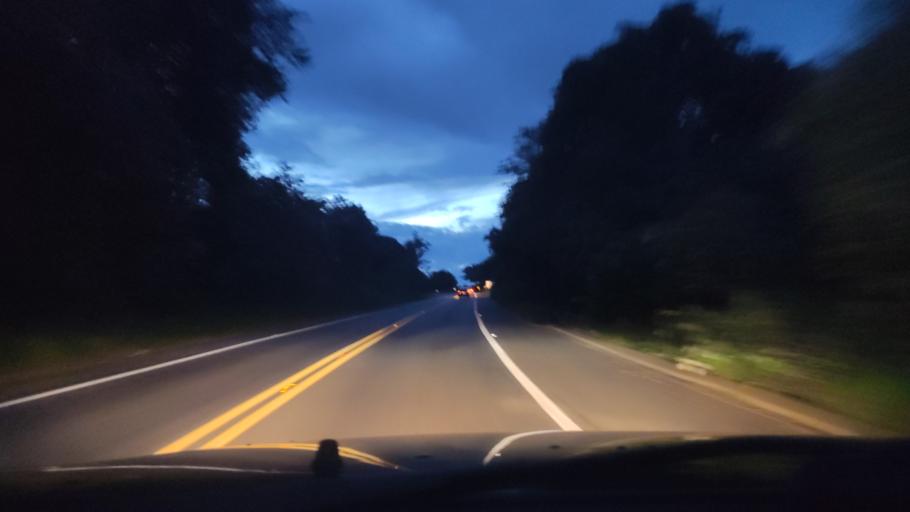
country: BR
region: Sao Paulo
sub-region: Socorro
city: Socorro
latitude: -22.5522
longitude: -46.5813
